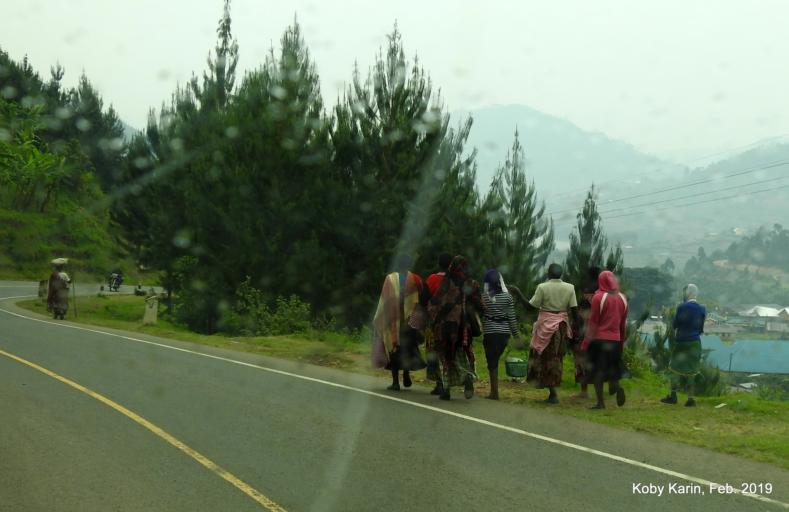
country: UG
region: Western Region
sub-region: Kisoro District
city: Kisoro
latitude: -1.2056
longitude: 29.8170
